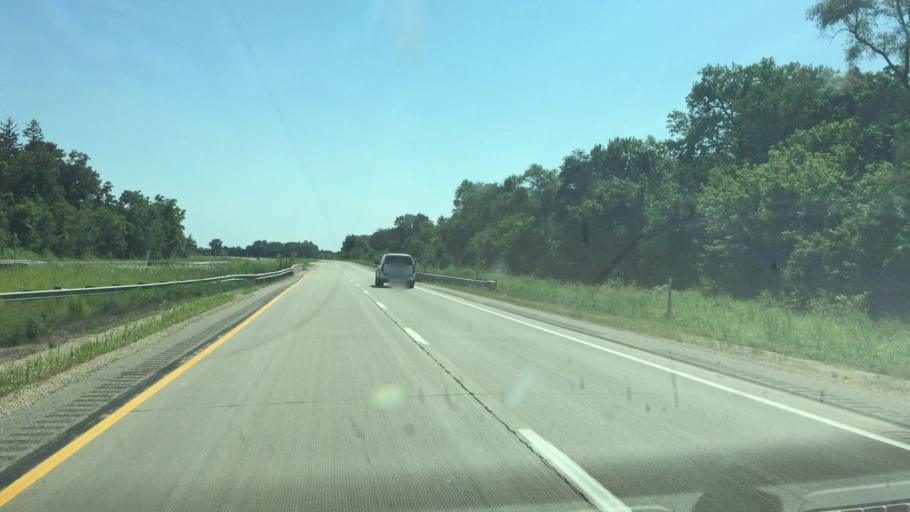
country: US
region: Iowa
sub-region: Jones County
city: Monticello
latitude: 42.2015
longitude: -91.2069
